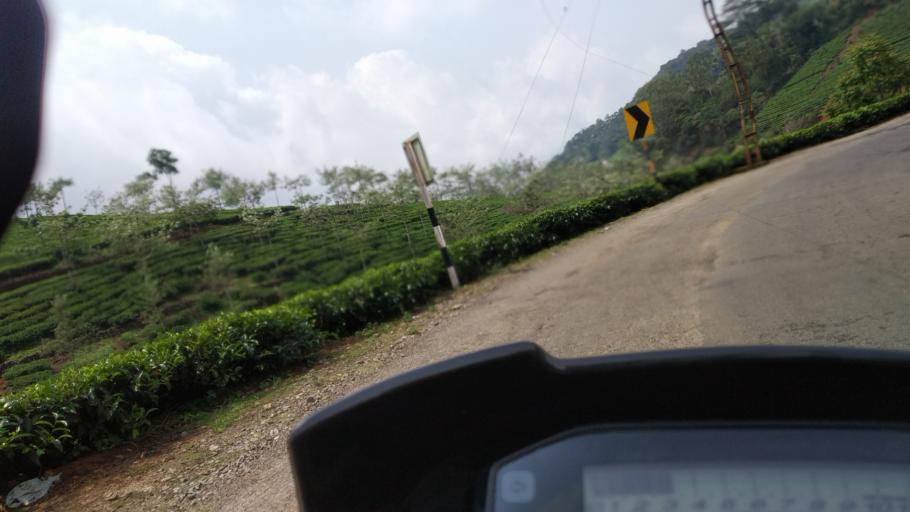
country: IN
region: Kerala
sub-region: Kottayam
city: Erattupetta
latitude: 9.6277
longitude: 76.9757
